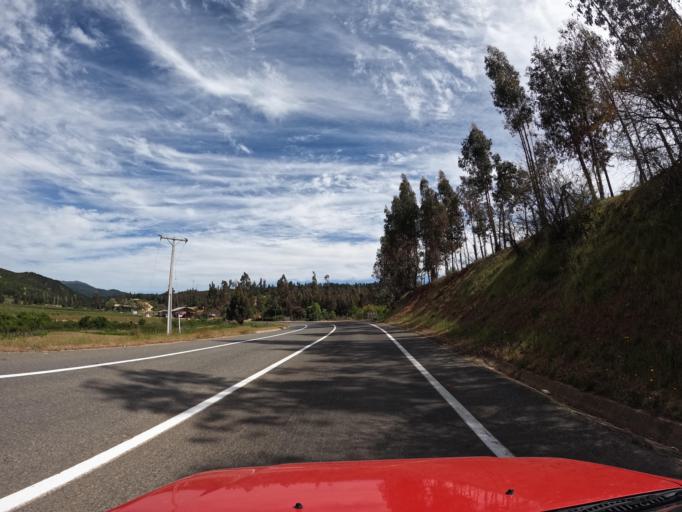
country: CL
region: Maule
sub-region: Provincia de Talca
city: Talca
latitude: -35.1473
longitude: -71.9635
